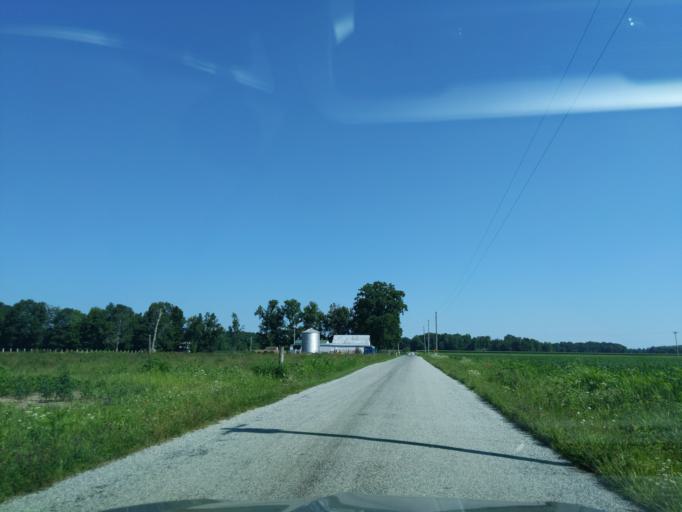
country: US
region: Indiana
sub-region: Ripley County
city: Osgood
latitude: 39.1085
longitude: -85.4322
